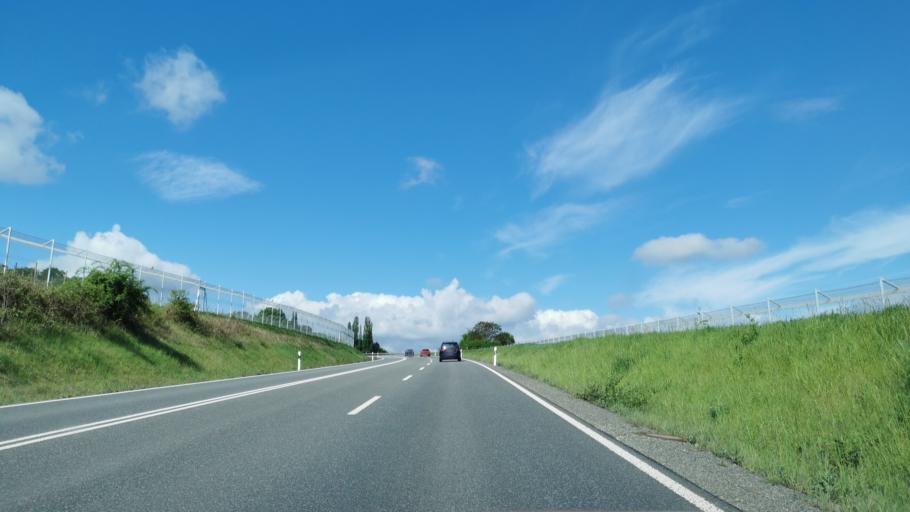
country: DE
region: Rheinland-Pfalz
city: Losnich
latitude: 49.9727
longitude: 7.0326
